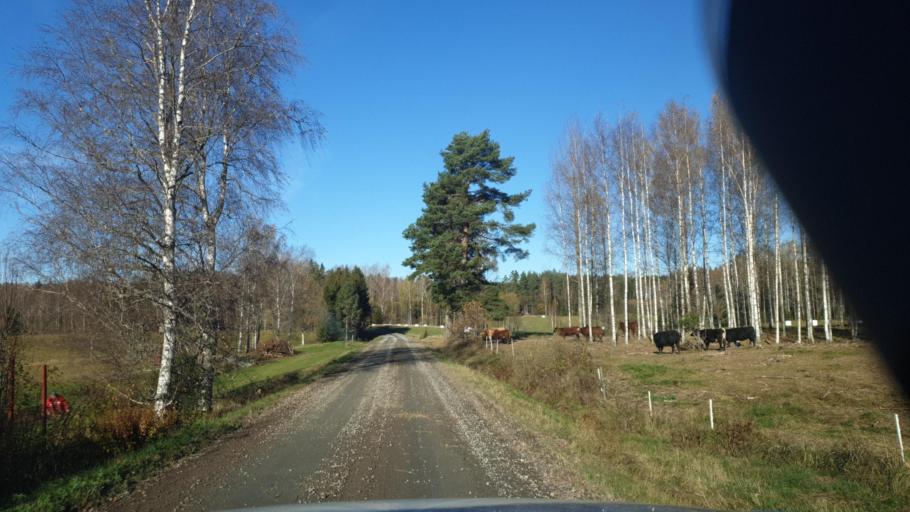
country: SE
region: Vaermland
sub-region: Karlstads Kommun
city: Edsvalla
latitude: 59.5108
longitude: 13.0186
